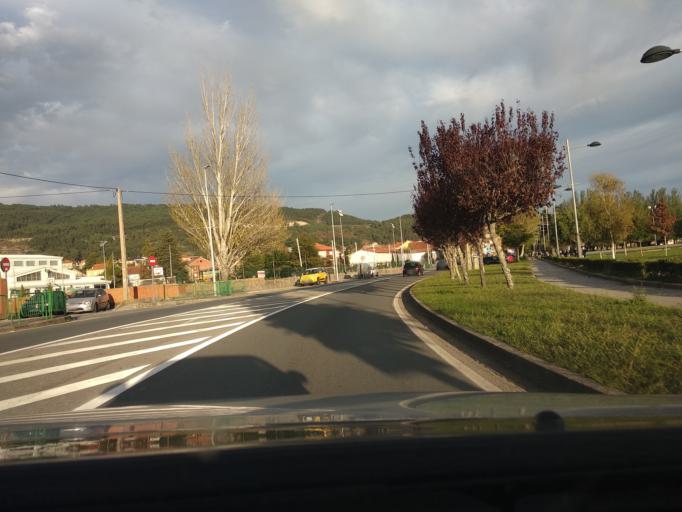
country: ES
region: Galicia
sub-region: Provincia de Pontevedra
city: Moana
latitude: 42.2879
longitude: -8.7296
